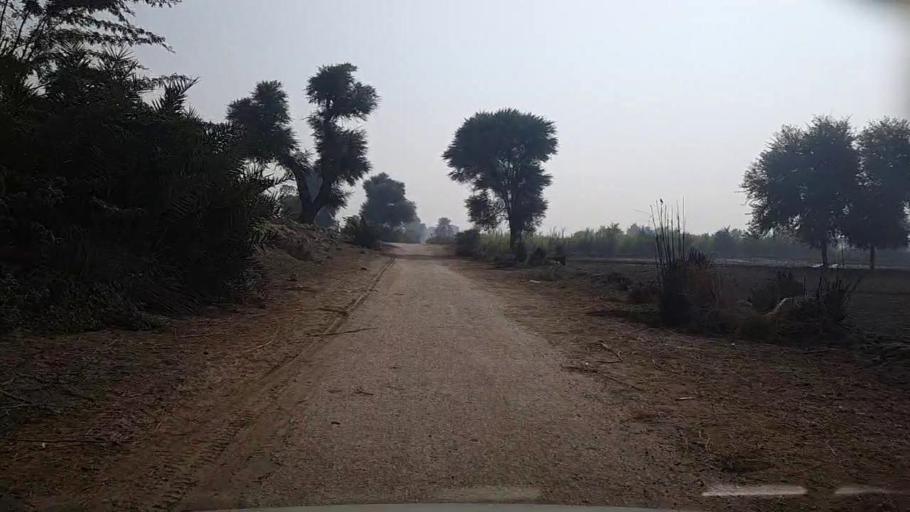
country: PK
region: Sindh
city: Setharja Old
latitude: 27.1364
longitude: 68.5108
